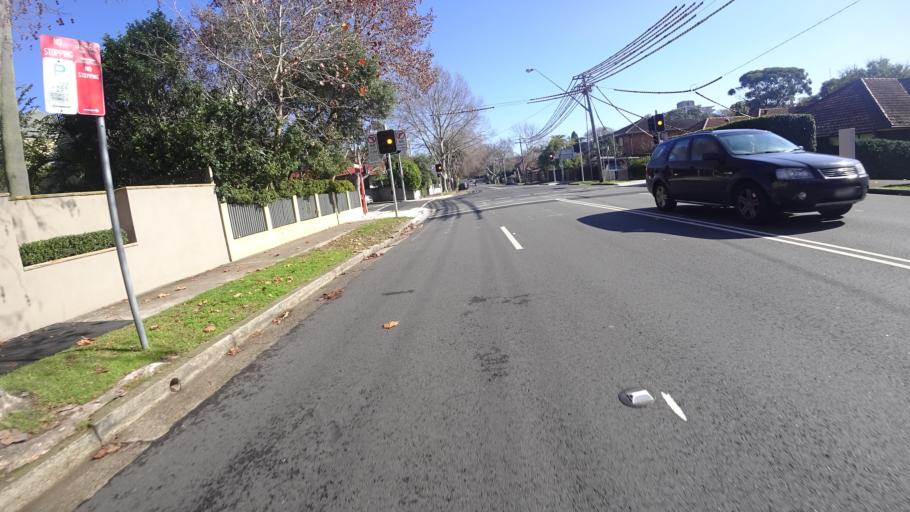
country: AU
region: New South Wales
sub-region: North Sydney
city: Crows Nest
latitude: -33.8225
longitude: 151.2035
